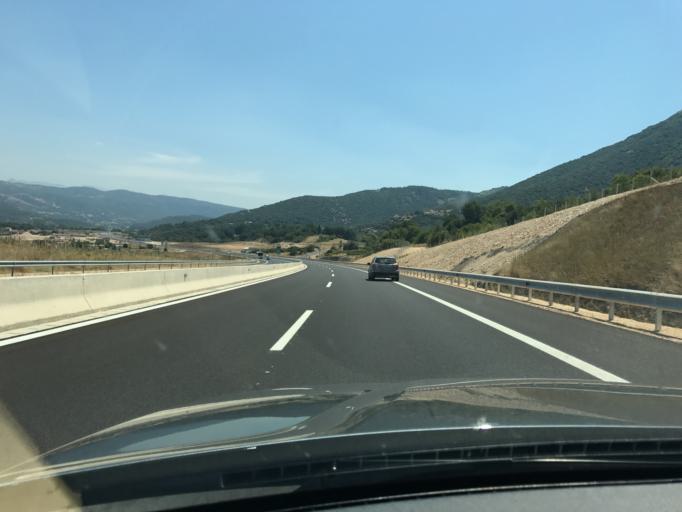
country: GR
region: Epirus
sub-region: Nomos Ioanninon
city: Pedini
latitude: 39.5498
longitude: 20.8402
